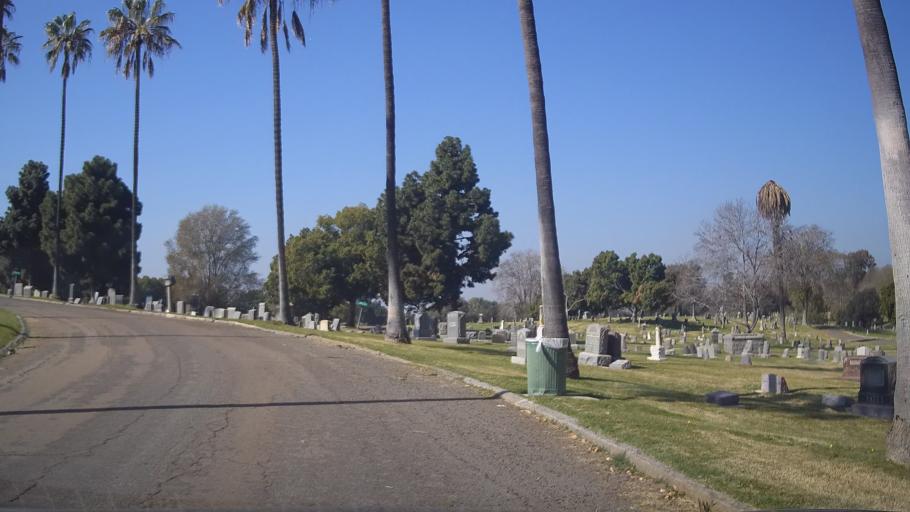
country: US
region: California
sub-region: San Diego County
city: National City
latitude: 32.7058
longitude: -117.1106
